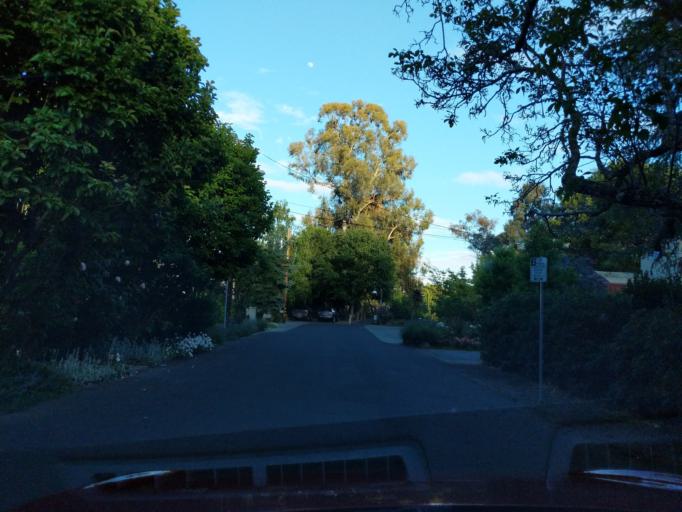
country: US
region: California
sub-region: San Mateo County
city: Menlo Park
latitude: 37.4400
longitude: -122.1806
